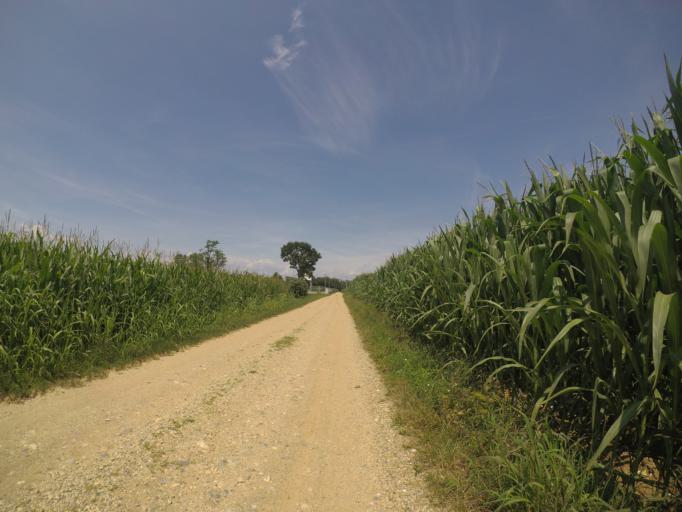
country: IT
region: Friuli Venezia Giulia
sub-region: Provincia di Udine
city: Bertiolo
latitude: 45.9718
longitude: 13.0959
